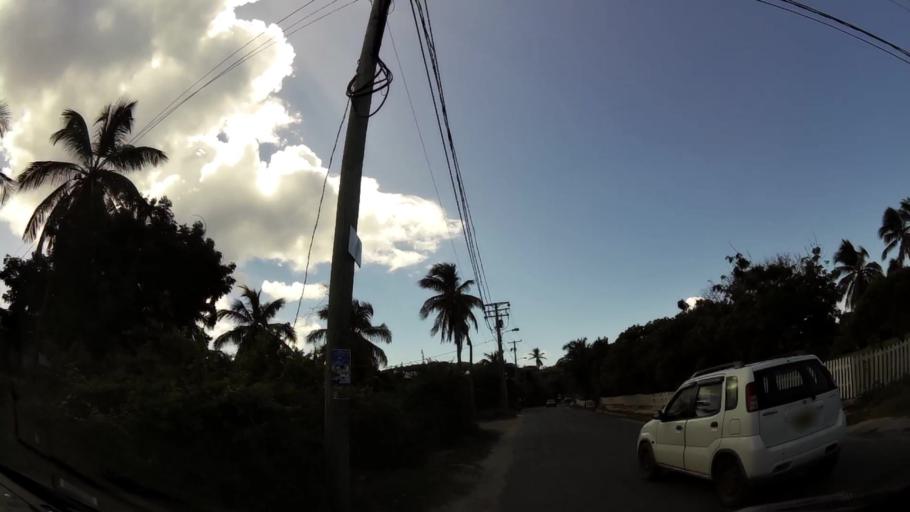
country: VG
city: Tortola
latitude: 18.4451
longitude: -64.4378
